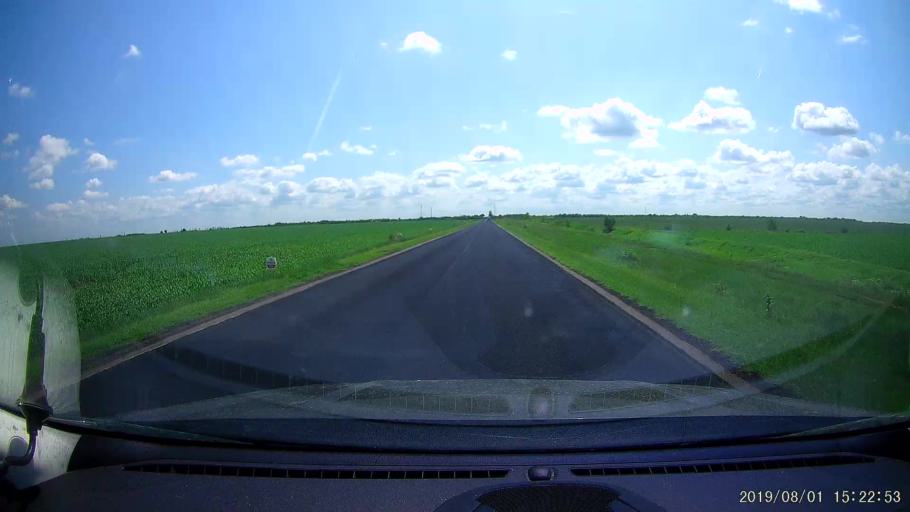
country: RO
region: Braila
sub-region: Comuna Viziru
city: Lanurile
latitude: 45.0479
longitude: 27.7691
